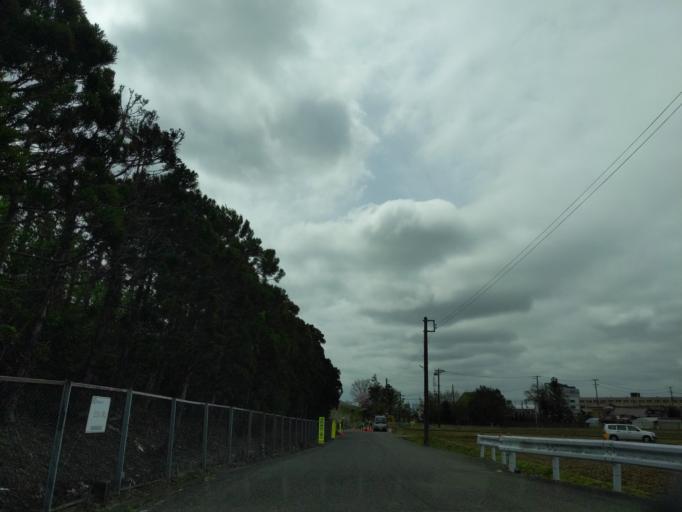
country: JP
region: Fukushima
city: Koriyama
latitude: 37.3842
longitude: 140.3124
